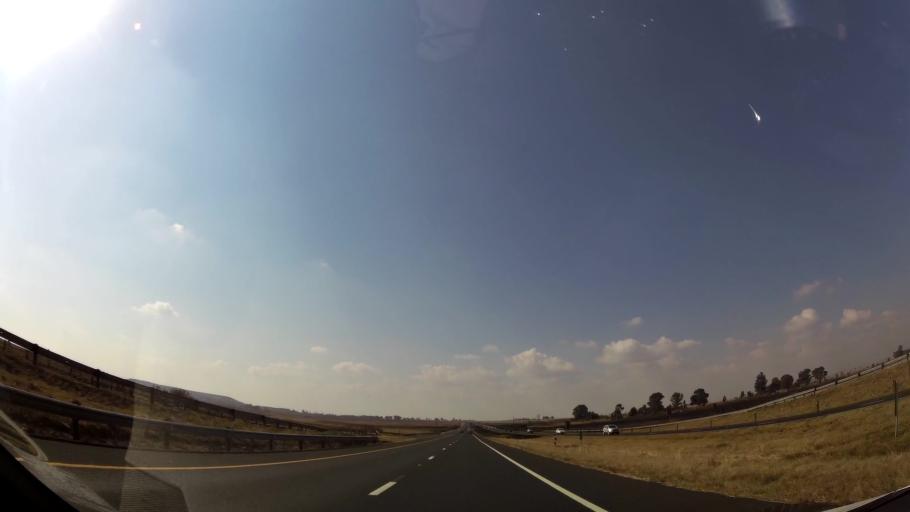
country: ZA
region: Gauteng
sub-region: Ekurhuleni Metropolitan Municipality
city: Springs
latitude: -26.1639
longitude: 28.4963
